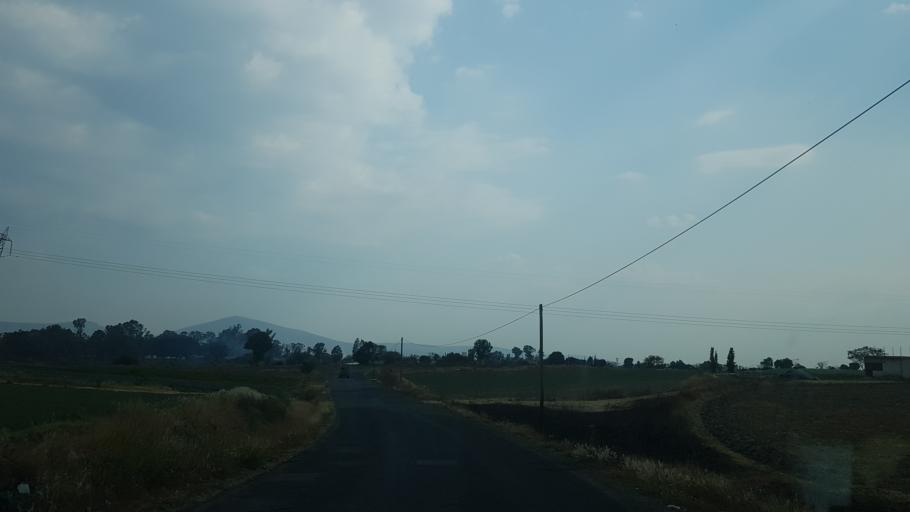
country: MX
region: Puebla
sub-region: Santa Isabel Cholula
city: Santa Ana Acozautla
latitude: 18.9541
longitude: -98.3944
